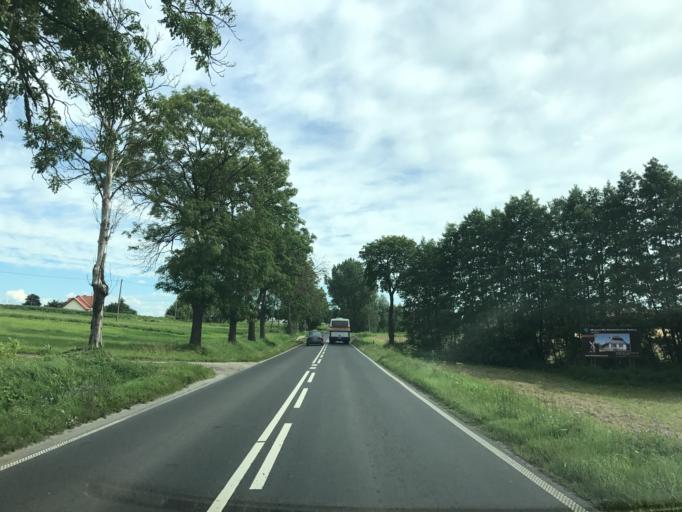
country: PL
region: Kujawsko-Pomorskie
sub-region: Powiat rypinski
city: Rypin
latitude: 53.1046
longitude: 19.3921
